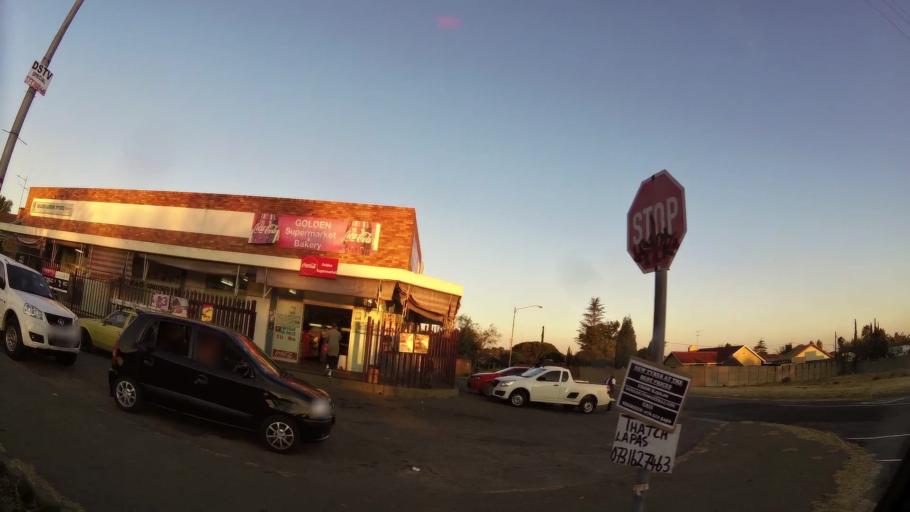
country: ZA
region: Gauteng
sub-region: Ekurhuleni Metropolitan Municipality
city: Germiston
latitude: -26.2711
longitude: 28.1532
